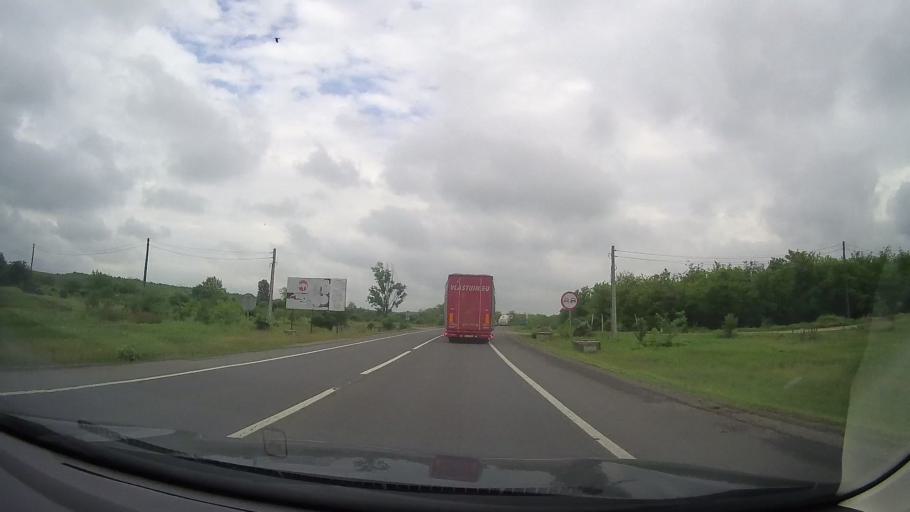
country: RO
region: Dolj
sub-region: Comuna Simnicu de Sus
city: Simnicu de Sus
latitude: 44.3520
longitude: 23.8248
